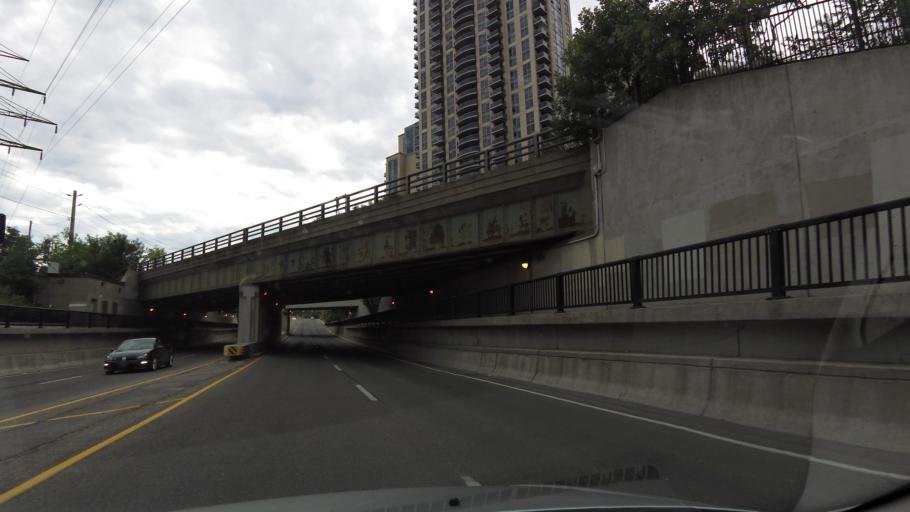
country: CA
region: Ontario
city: Etobicoke
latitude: 43.6438
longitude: -79.5272
